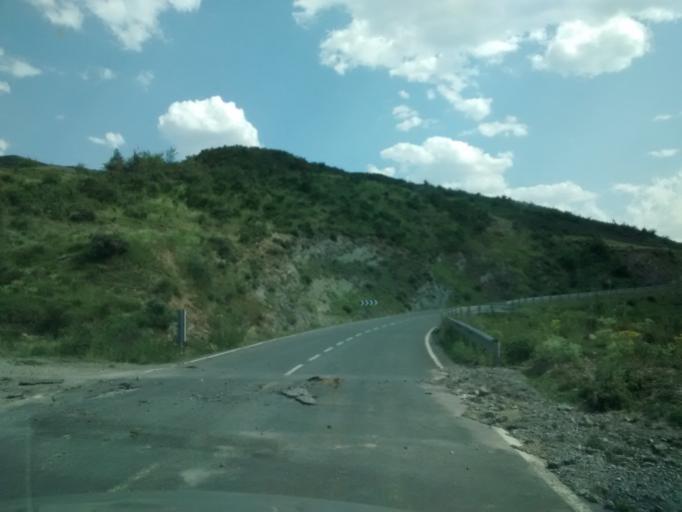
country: ES
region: La Rioja
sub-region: Provincia de La Rioja
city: Jalon de Cameros
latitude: 42.2149
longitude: -2.4769
